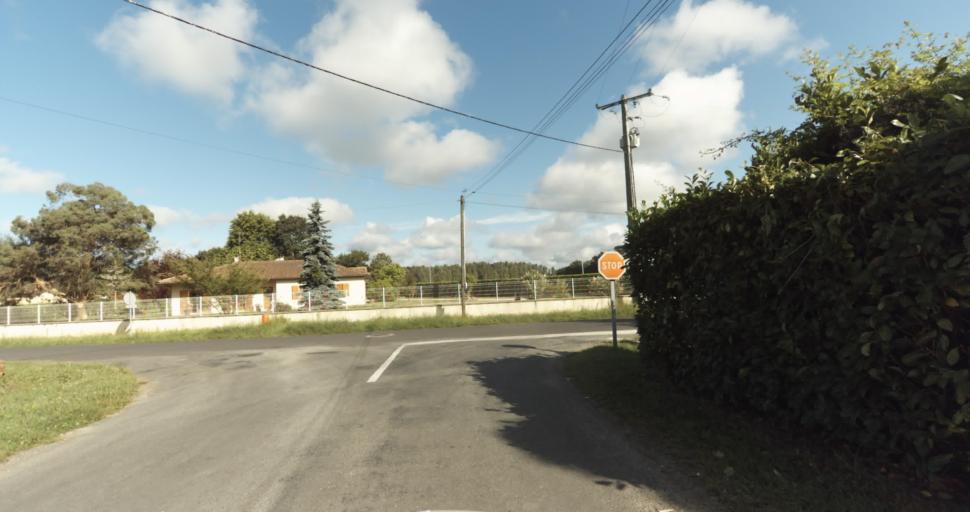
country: FR
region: Aquitaine
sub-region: Departement de la Gironde
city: Bazas
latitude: 44.4419
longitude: -0.2448
